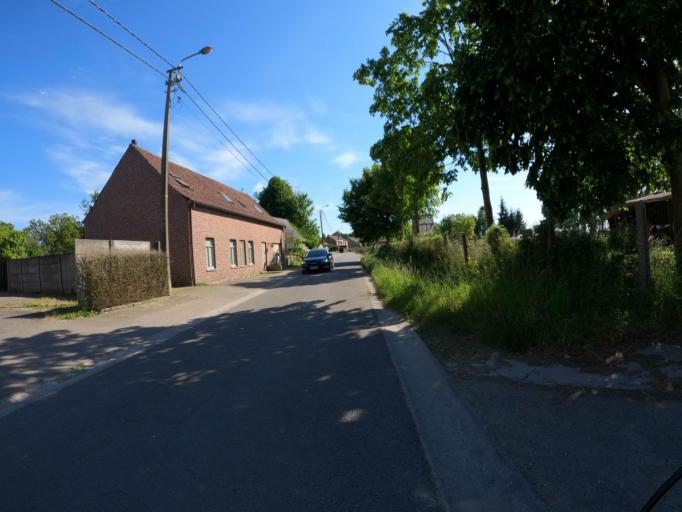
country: BE
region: Flanders
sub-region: Provincie Oost-Vlaanderen
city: Oosterzele
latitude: 50.9230
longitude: 3.7845
